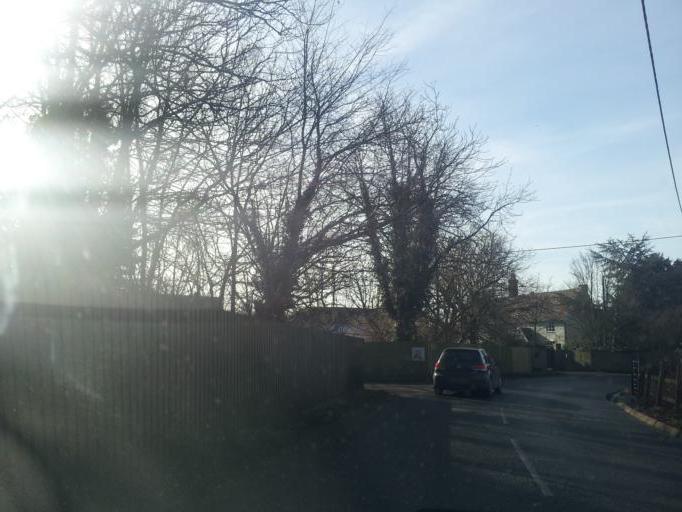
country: GB
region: England
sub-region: Suffolk
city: Wickham Market
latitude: 52.1568
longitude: 1.3053
